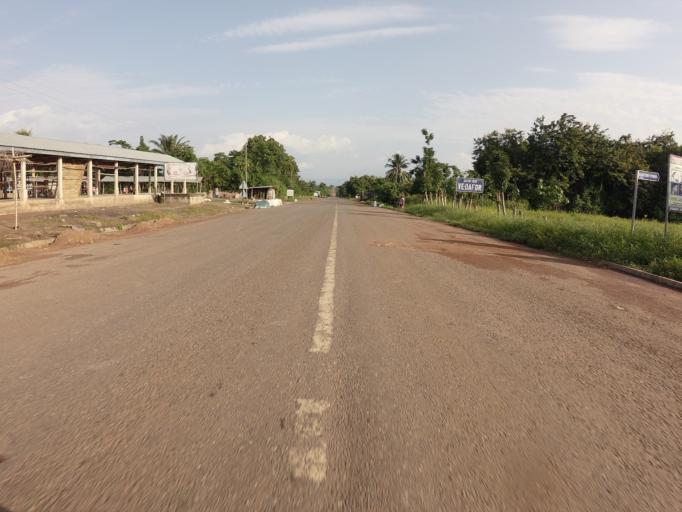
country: GH
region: Volta
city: Hohoe
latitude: 7.0427
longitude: 0.4266
